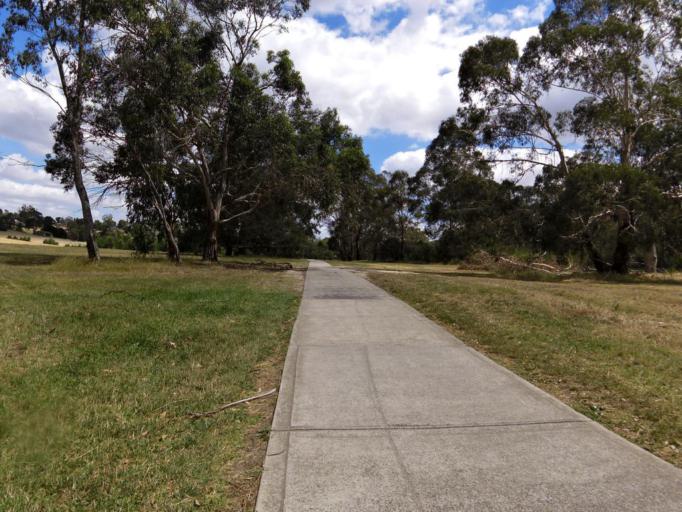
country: AU
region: Victoria
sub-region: Nillumbik
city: Eltham North
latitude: -37.6844
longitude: 145.1532
